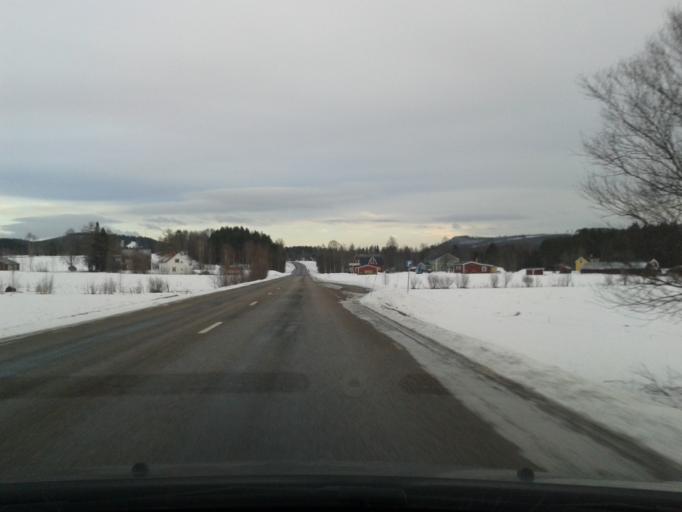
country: SE
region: Vaesternorrland
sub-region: Solleftea Kommun
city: As
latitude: 63.4561
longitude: 16.8942
